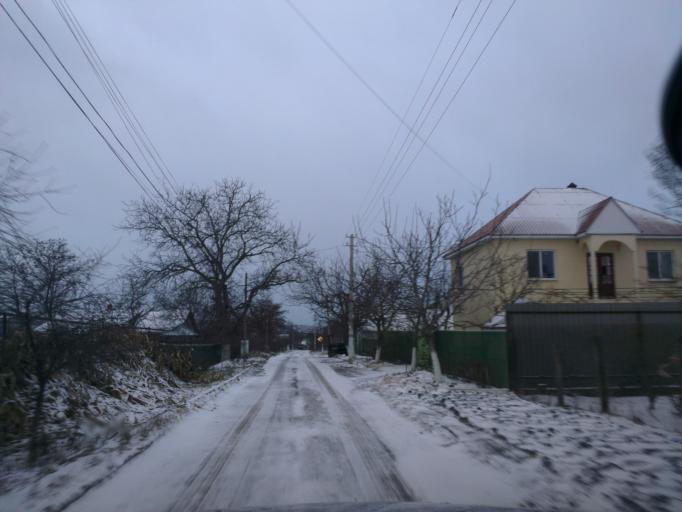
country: MD
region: Chisinau
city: Ciorescu
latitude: 47.1149
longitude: 28.9037
